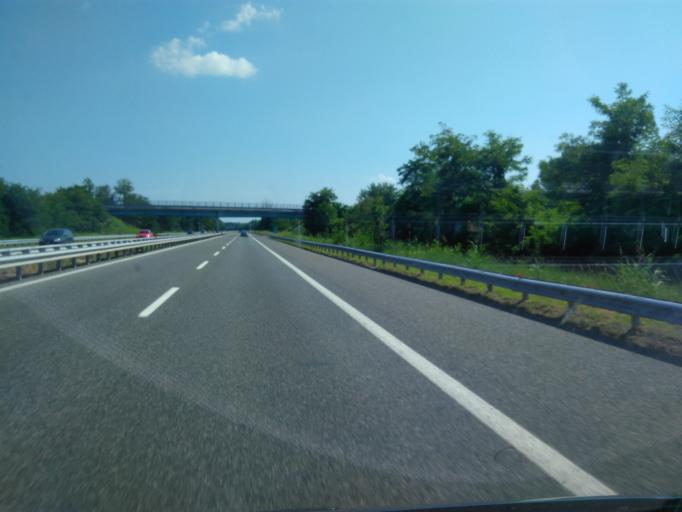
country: IT
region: Piedmont
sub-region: Provincia di Novara
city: Ghemme
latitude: 45.5905
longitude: 8.4033
